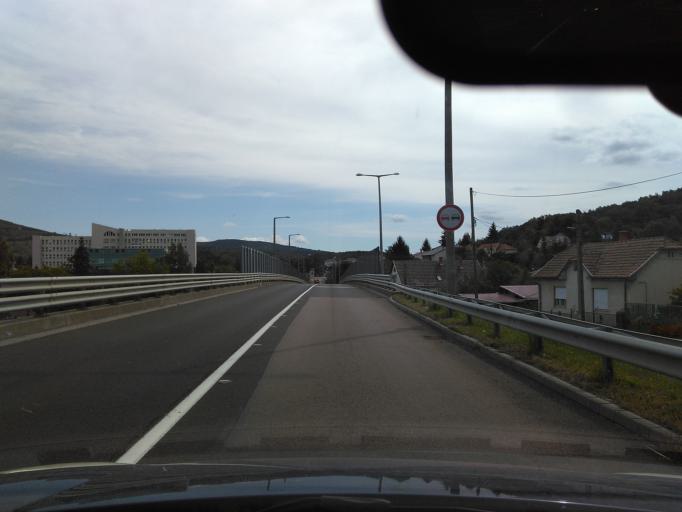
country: HU
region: Nograd
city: Salgotarjan
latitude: 48.1174
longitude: 19.8068
